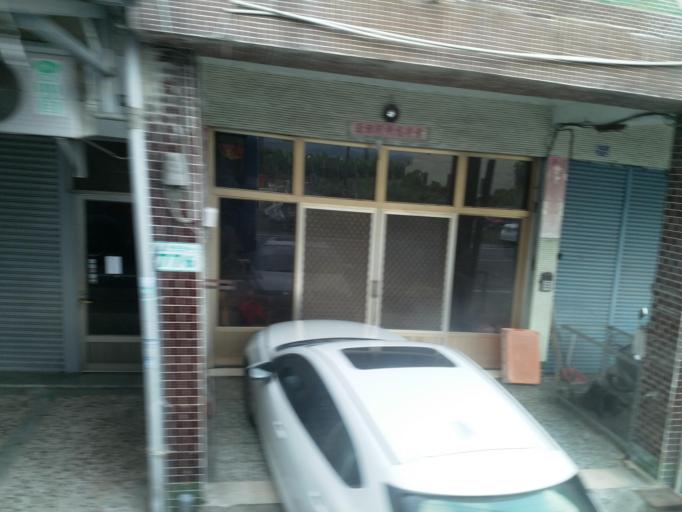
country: TW
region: Taiwan
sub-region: Pingtung
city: Pingtung
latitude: 22.8679
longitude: 120.5365
